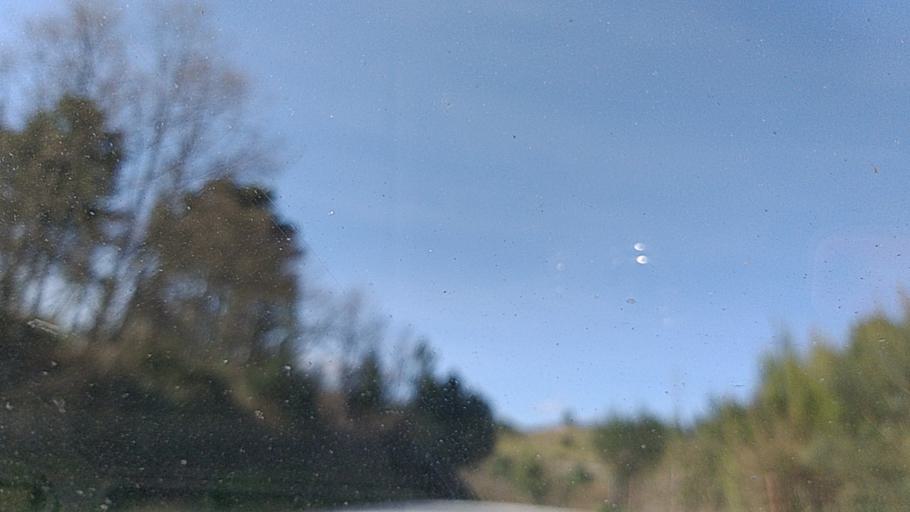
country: PT
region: Guarda
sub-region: Celorico da Beira
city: Celorico da Beira
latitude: 40.6462
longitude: -7.3955
